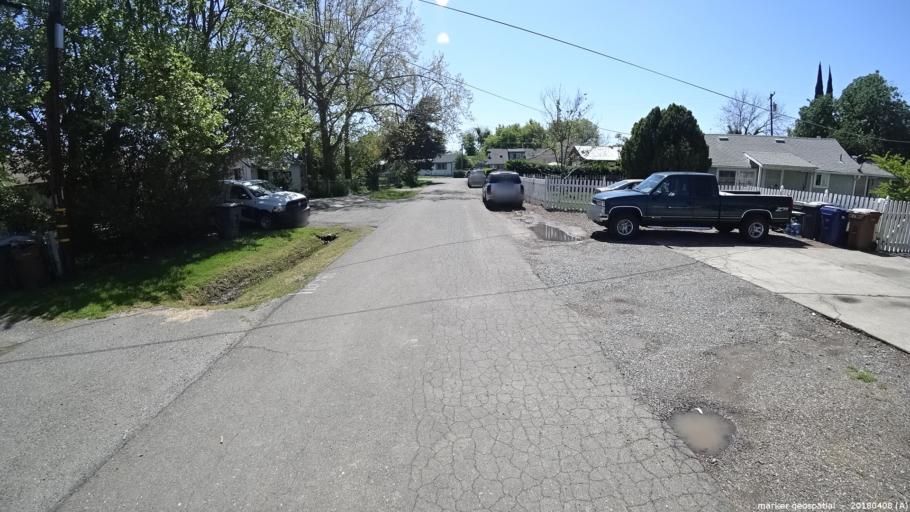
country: US
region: California
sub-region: Sacramento County
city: Laguna
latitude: 38.3674
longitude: -121.5168
